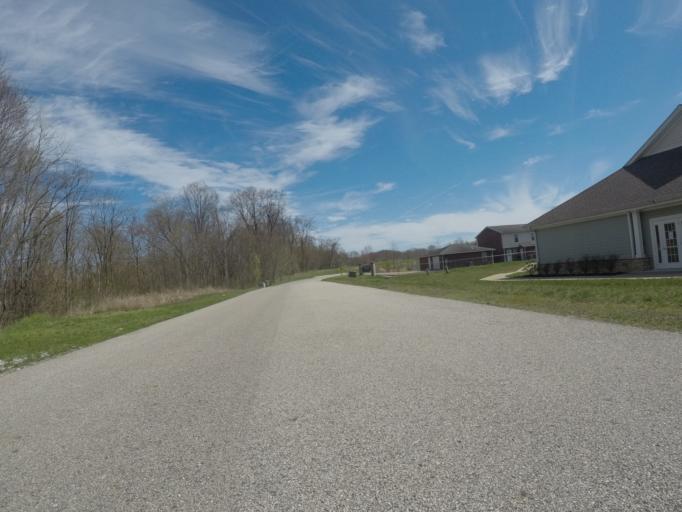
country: US
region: West Virginia
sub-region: Cabell County
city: Pea Ridge
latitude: 38.4107
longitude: -82.3090
